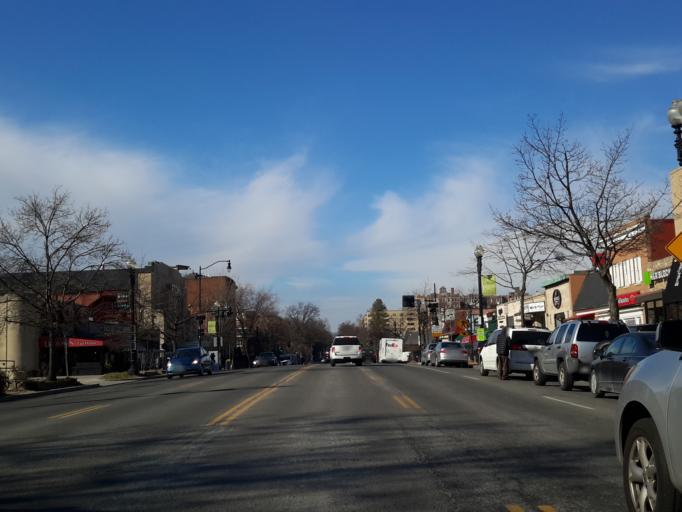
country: US
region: Maryland
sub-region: Montgomery County
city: Chevy Chase Village
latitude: 38.9341
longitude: -77.0576
